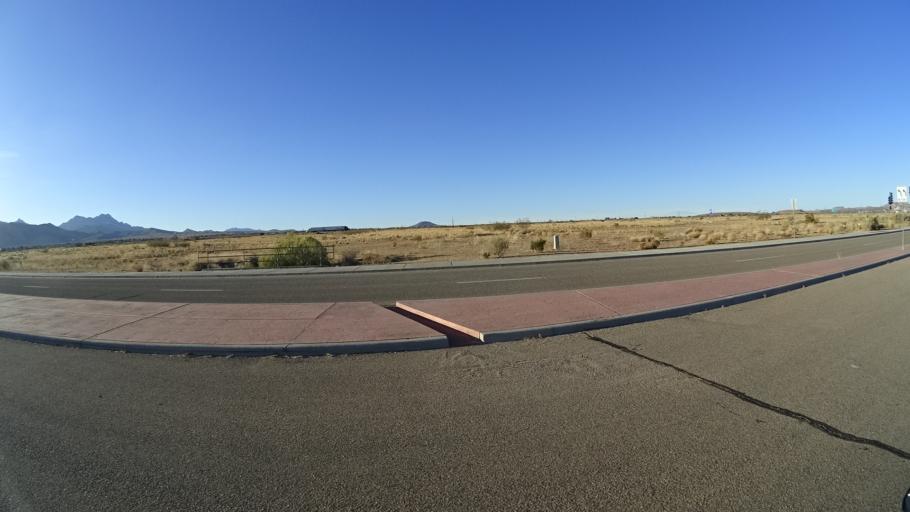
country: US
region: Arizona
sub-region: Mohave County
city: New Kingman-Butler
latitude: 35.2178
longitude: -113.9830
